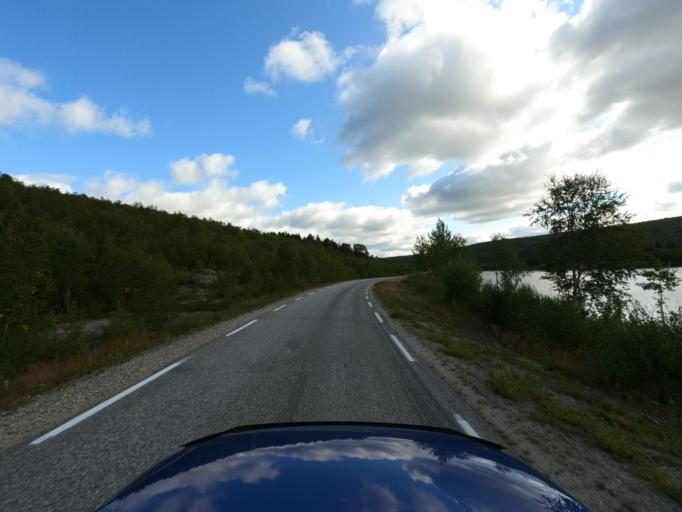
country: NO
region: Finnmark Fylke
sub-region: Porsanger
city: Lakselv
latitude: 69.4231
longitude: 24.8392
